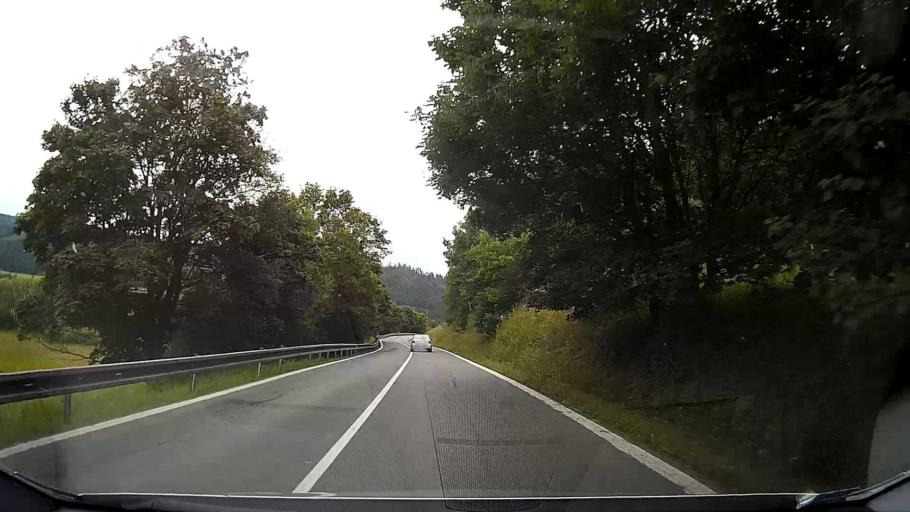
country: SK
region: Banskobystricky
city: Revuca
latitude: 48.8378
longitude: 20.1777
